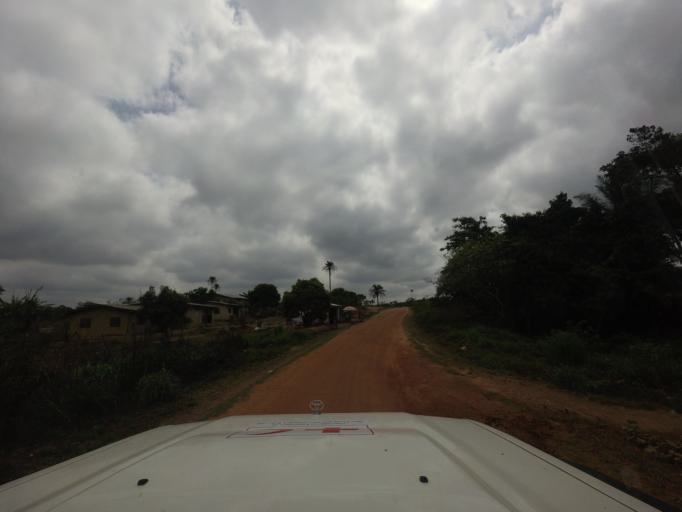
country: LR
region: Lofa
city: Voinjama
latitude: 8.4167
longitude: -9.7392
